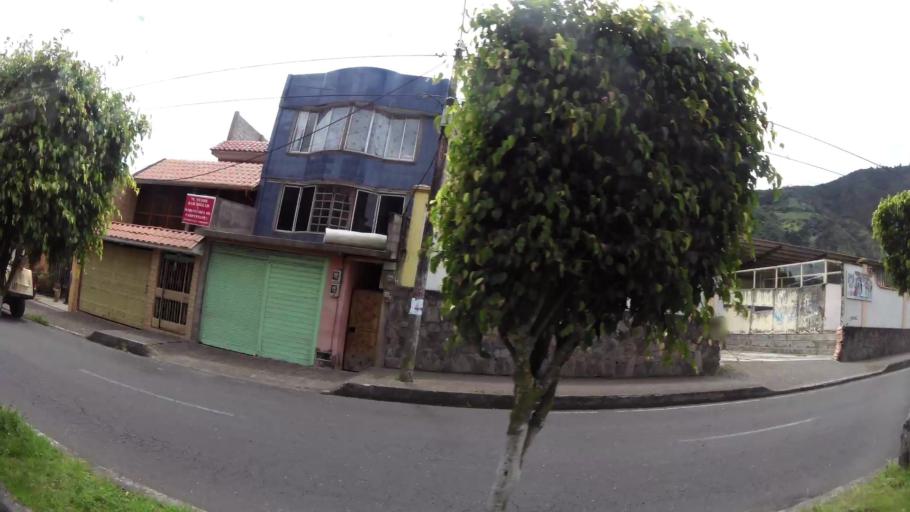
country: EC
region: Tungurahua
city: Banos
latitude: -1.3928
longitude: -78.4179
